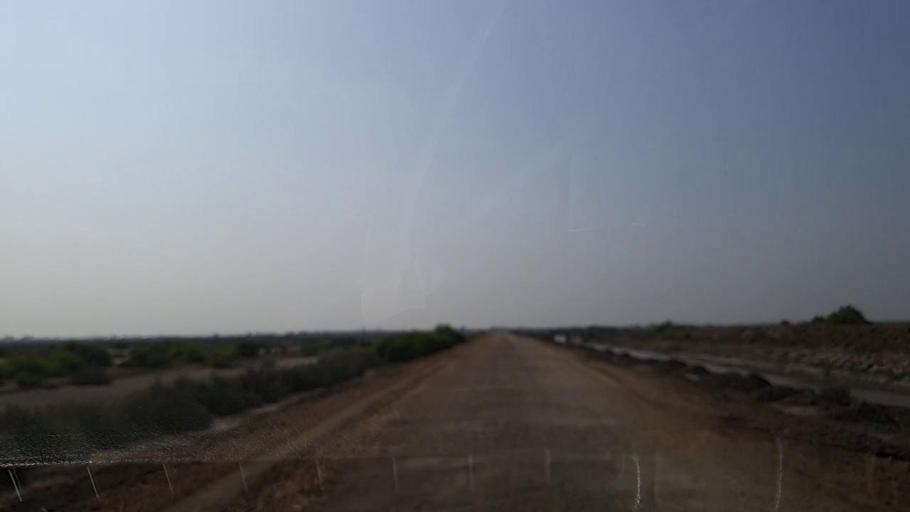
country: PK
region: Sindh
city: Mirpur Sakro
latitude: 24.6354
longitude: 67.7236
